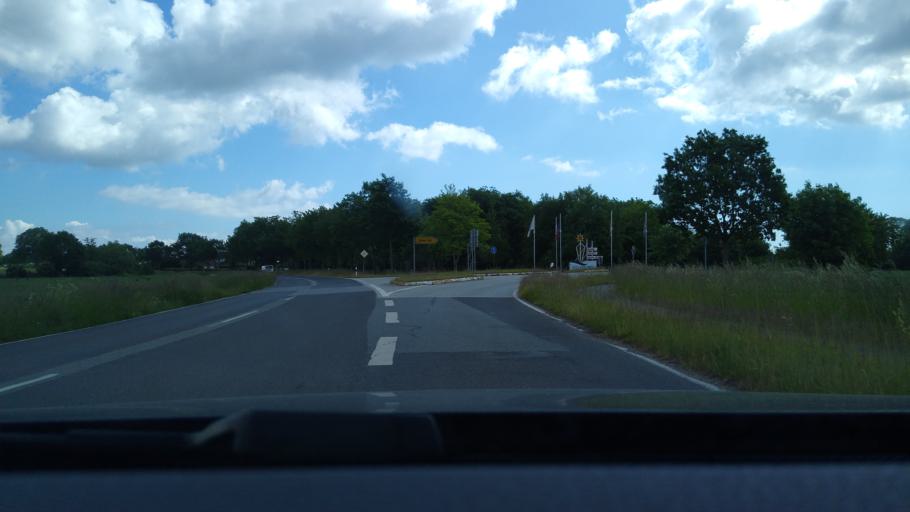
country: DE
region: Schleswig-Holstein
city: Dahme
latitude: 54.2152
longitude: 11.0729
